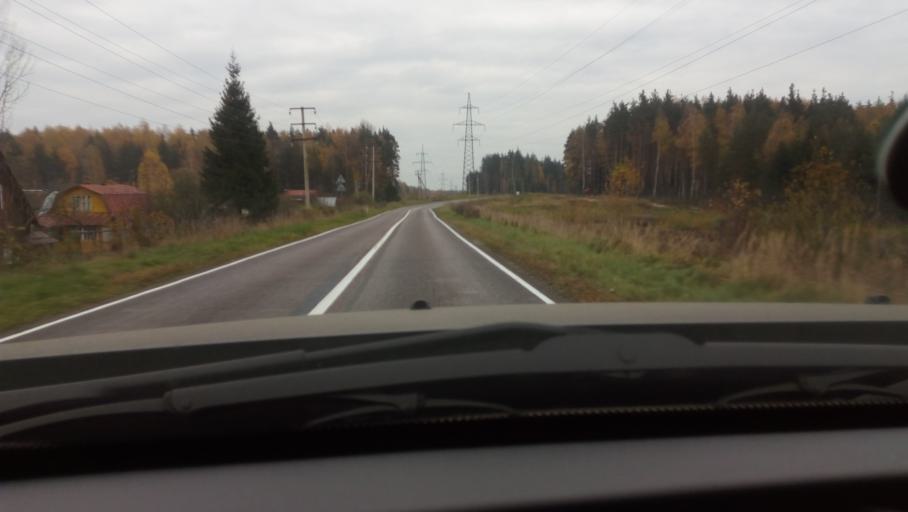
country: RU
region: Moskovskaya
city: Avsyunino
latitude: 55.6041
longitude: 39.1985
